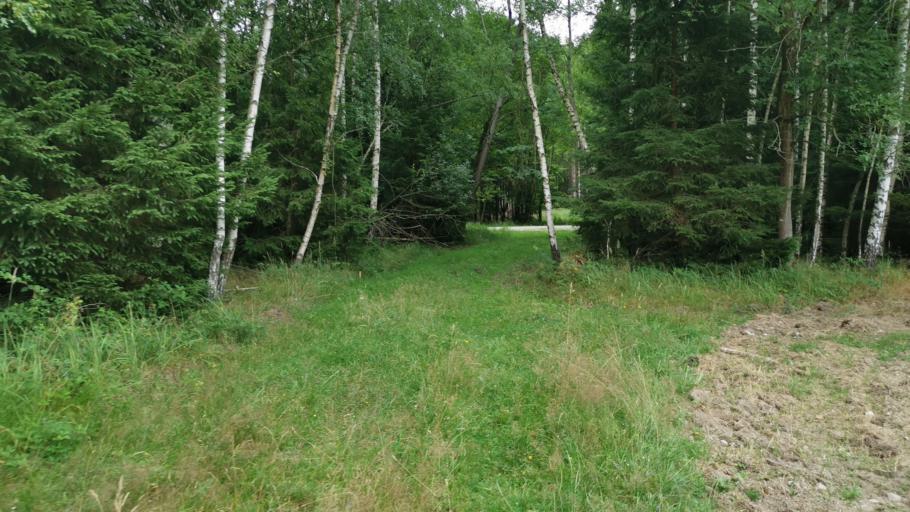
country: DE
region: Bavaria
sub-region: Upper Bavaria
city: Neuried
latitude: 48.0545
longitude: 11.4678
